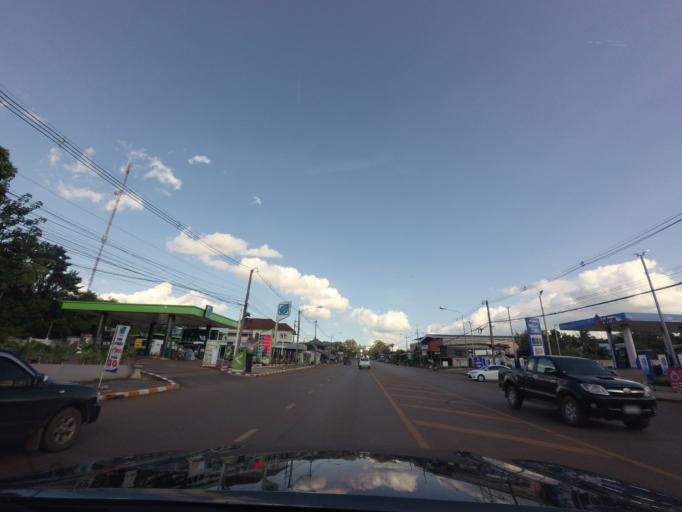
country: TH
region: Changwat Udon Thani
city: Ban Dung
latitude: 17.7031
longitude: 103.2554
